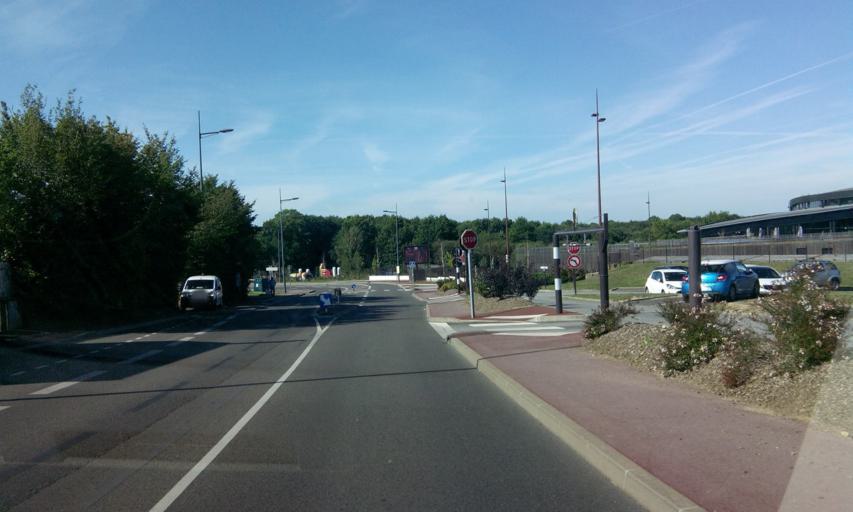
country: FR
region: Limousin
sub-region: Departement de la Haute-Vienne
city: Limoges
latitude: 45.8565
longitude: 1.2843
